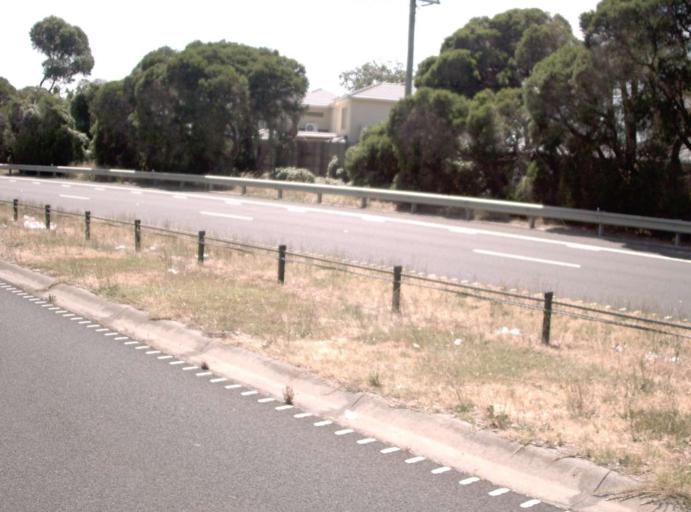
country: AU
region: Victoria
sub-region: Frankston
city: Frankston East
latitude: -38.1347
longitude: 145.1366
